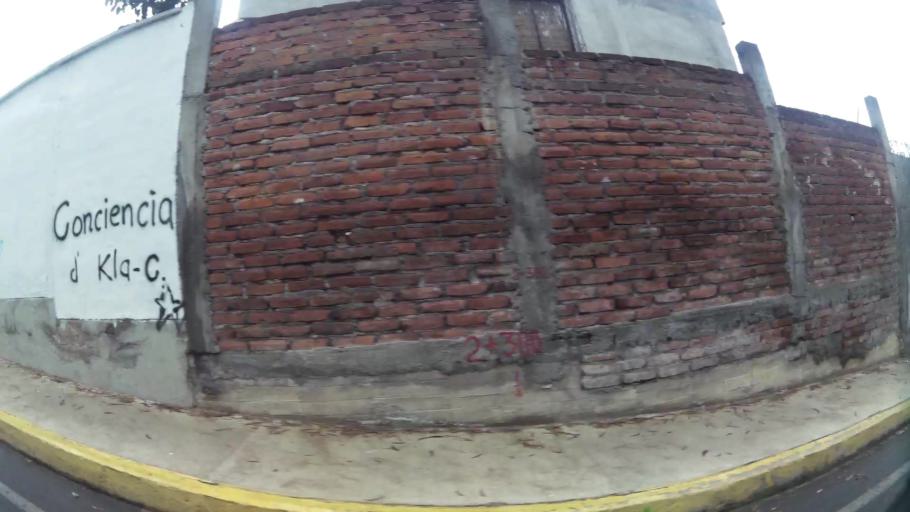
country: EC
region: Pichincha
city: Quito
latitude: -0.2660
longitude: -78.4732
